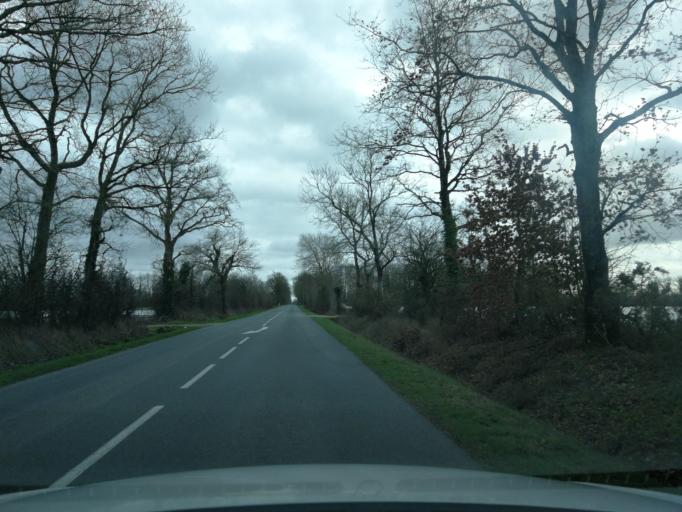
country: FR
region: Pays de la Loire
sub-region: Departement de la Loire-Atlantique
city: Geneston
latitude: 47.0350
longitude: -1.5045
